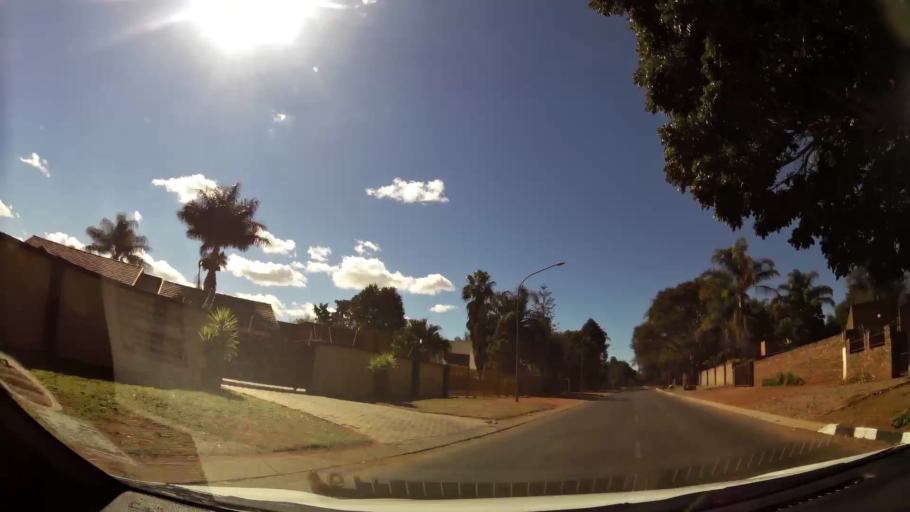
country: ZA
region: Limpopo
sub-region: Capricorn District Municipality
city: Polokwane
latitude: -23.9111
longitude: 29.4864
